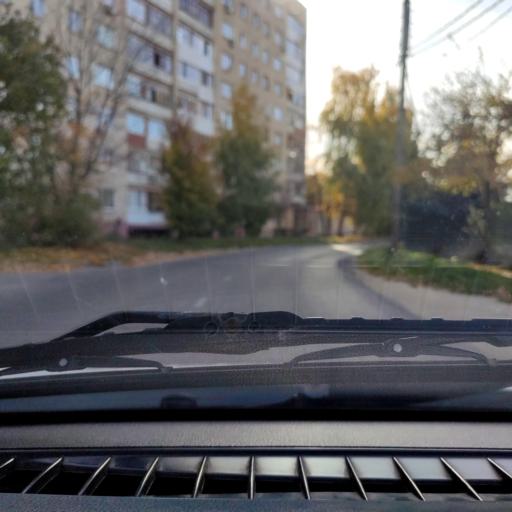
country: RU
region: Samara
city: Tol'yatti
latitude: 53.5074
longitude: 49.3989
